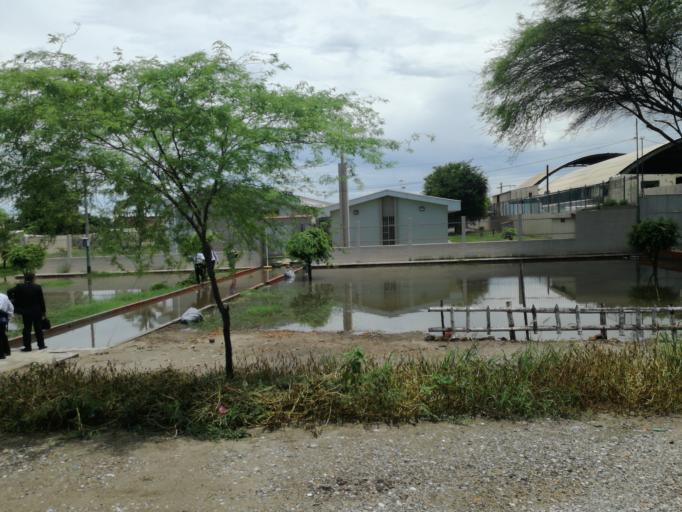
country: PE
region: Piura
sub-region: Provincia de Piura
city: Catacaos
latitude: -5.2625
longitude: -80.6688
